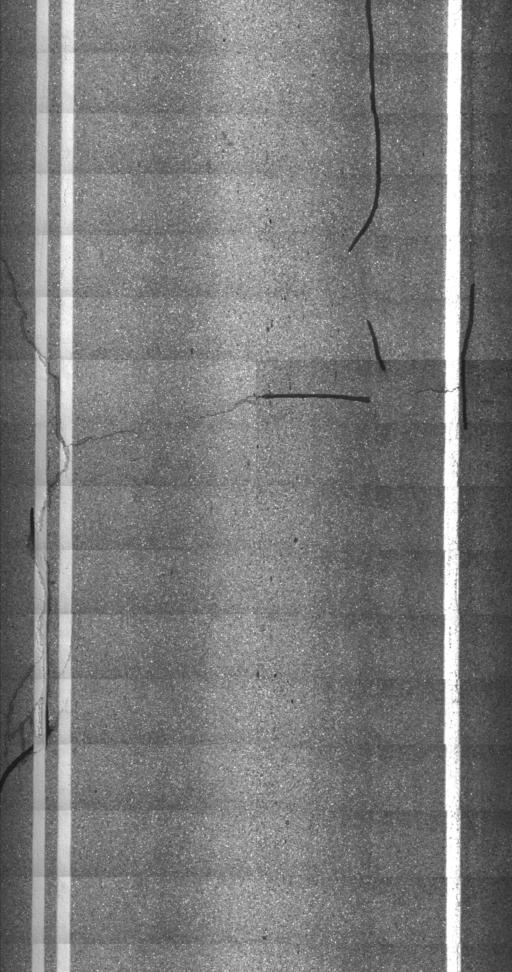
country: US
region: Vermont
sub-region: Windham County
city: Dover
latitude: 42.9402
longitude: -72.8549
